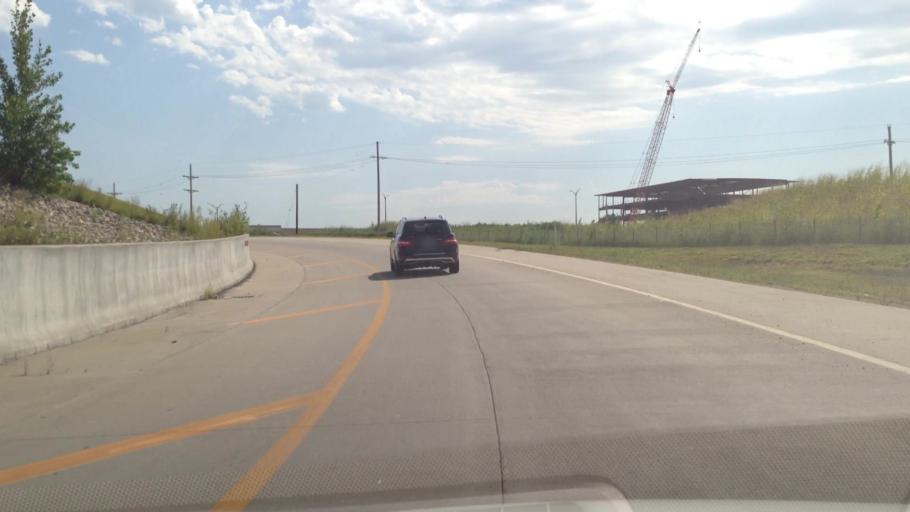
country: US
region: Kansas
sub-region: Johnson County
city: Lenexa
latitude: 38.9268
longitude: -94.7062
